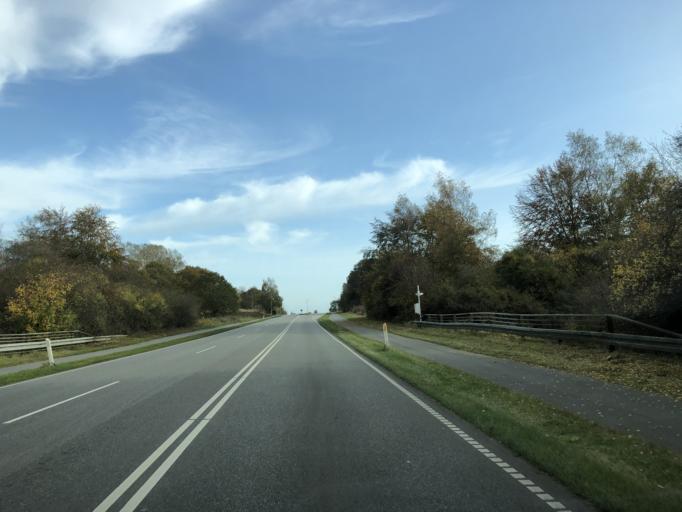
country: DK
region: Capital Region
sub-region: Allerod Kommune
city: Blovstrod
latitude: 55.8596
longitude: 12.3984
